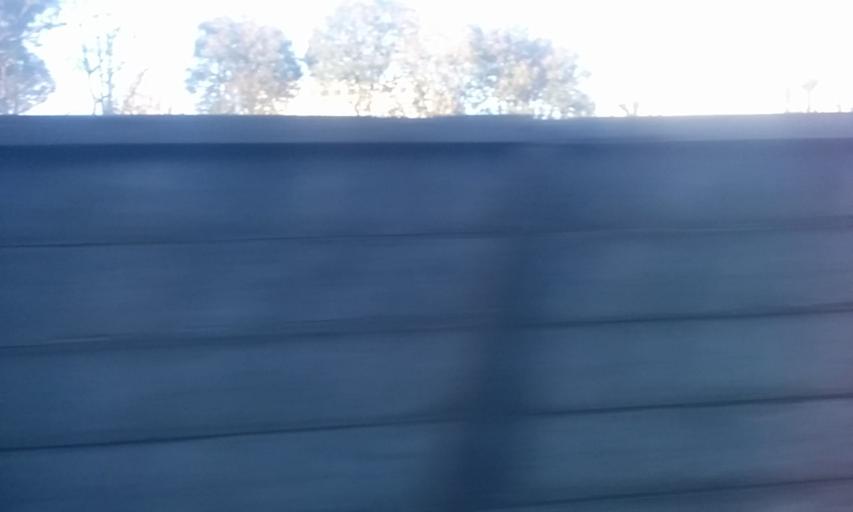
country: JP
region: Saitama
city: Kawaguchi
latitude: 35.7510
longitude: 139.7008
